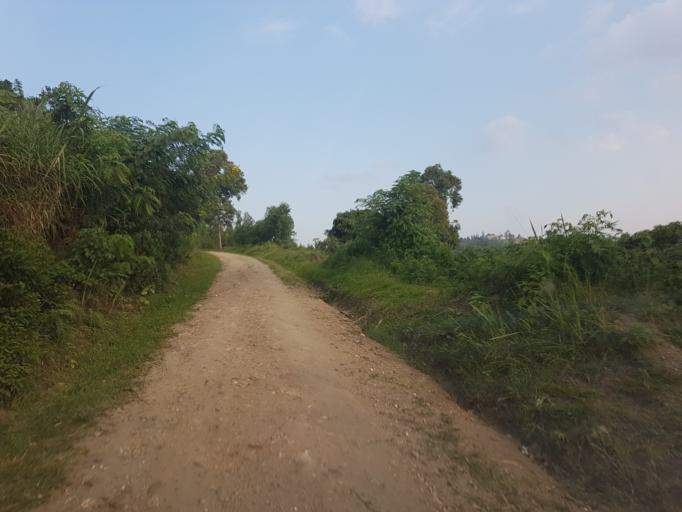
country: UG
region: Western Region
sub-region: Mitoma District
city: Mitoma
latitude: -0.6787
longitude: 29.9042
